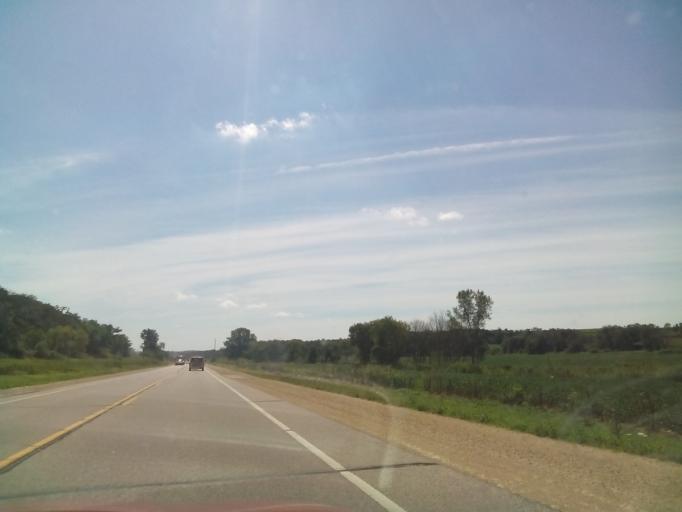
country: US
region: Wisconsin
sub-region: Green County
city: Monticello
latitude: 42.7701
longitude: -89.6263
